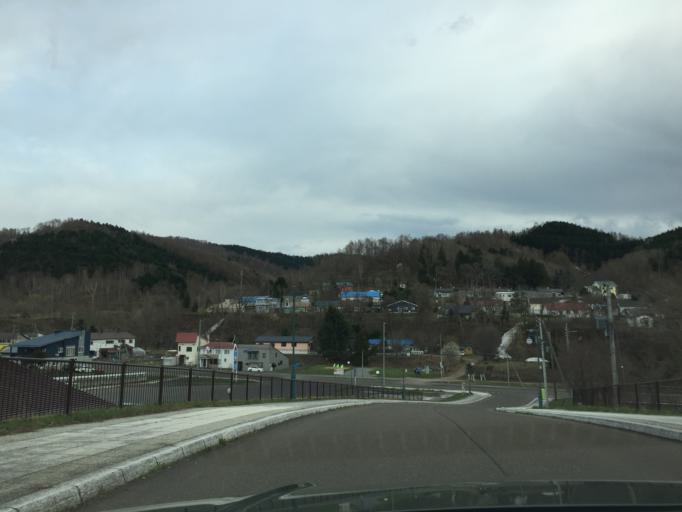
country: JP
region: Hokkaido
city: Utashinai
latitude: 43.5034
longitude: 142.0053
